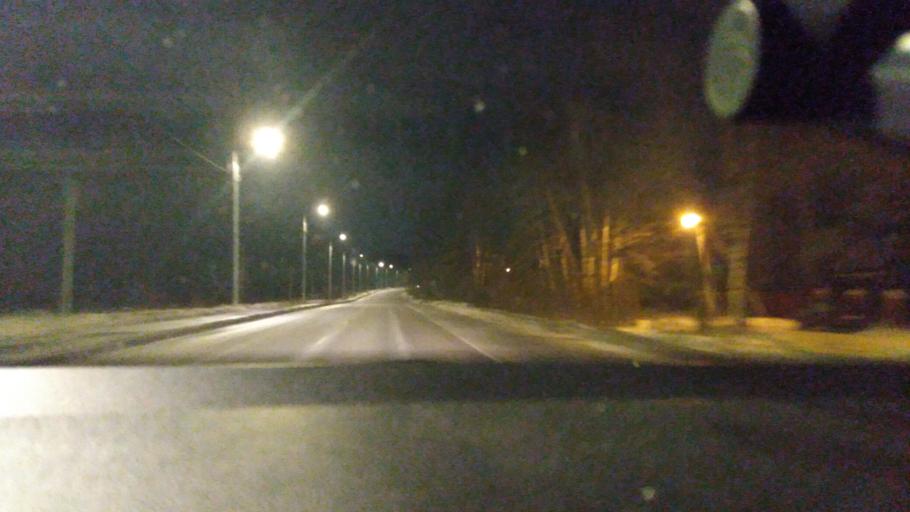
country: RU
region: Moskovskaya
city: Yegor'yevsk
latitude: 55.3541
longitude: 39.0733
